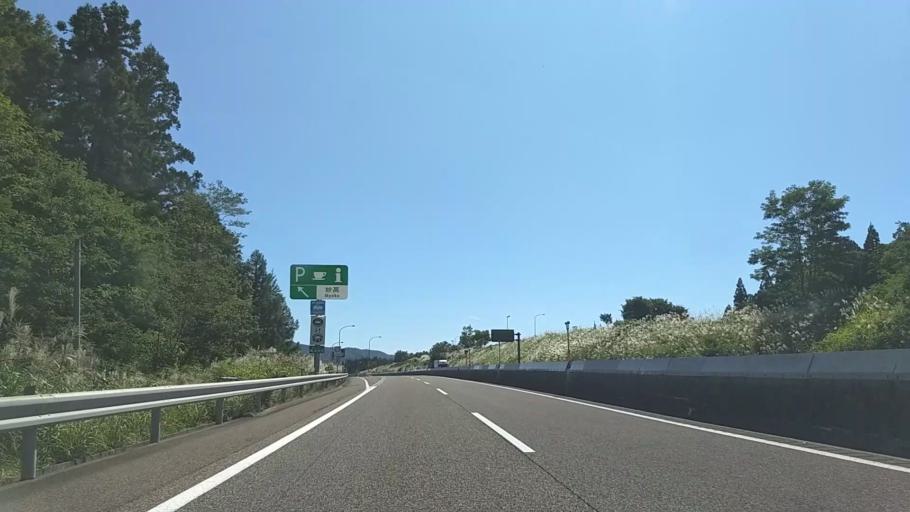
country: JP
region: Niigata
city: Arai
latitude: 36.9324
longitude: 138.2120
